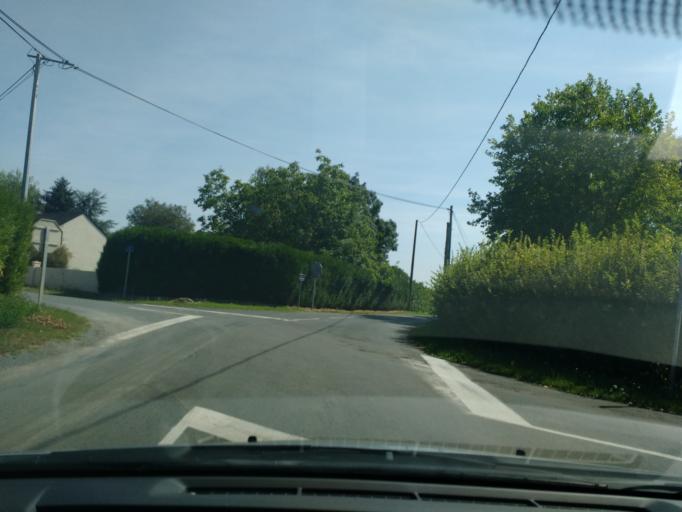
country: FR
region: Pays de la Loire
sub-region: Departement de Maine-et-Loire
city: Maze
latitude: 47.4735
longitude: -0.2719
